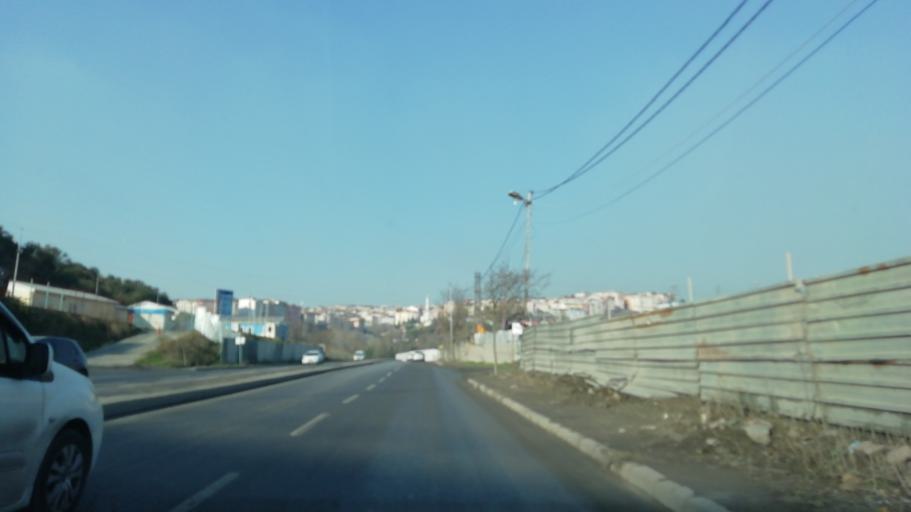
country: TR
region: Istanbul
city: Sultangazi
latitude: 41.0951
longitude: 28.9201
